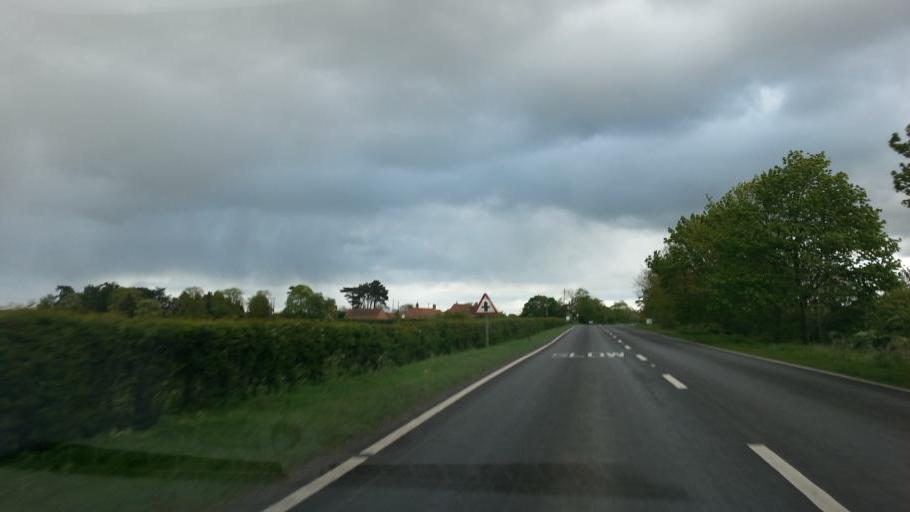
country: GB
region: England
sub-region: Nottinghamshire
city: Newark on Trent
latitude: 53.1063
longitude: -0.8469
